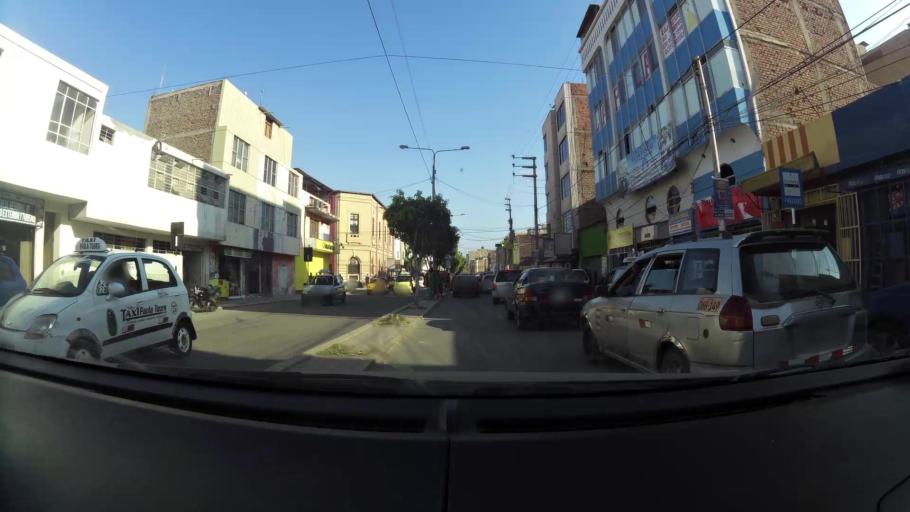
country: PE
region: Lambayeque
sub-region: Provincia de Chiclayo
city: Chiclayo
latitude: -6.7710
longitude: -79.8361
